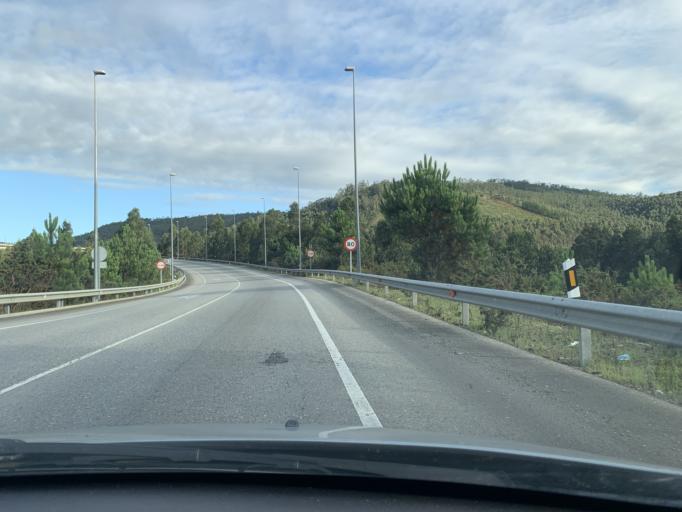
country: ES
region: Galicia
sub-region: Provincia de Lugo
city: Barreiros
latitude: 43.5337
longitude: -7.2547
